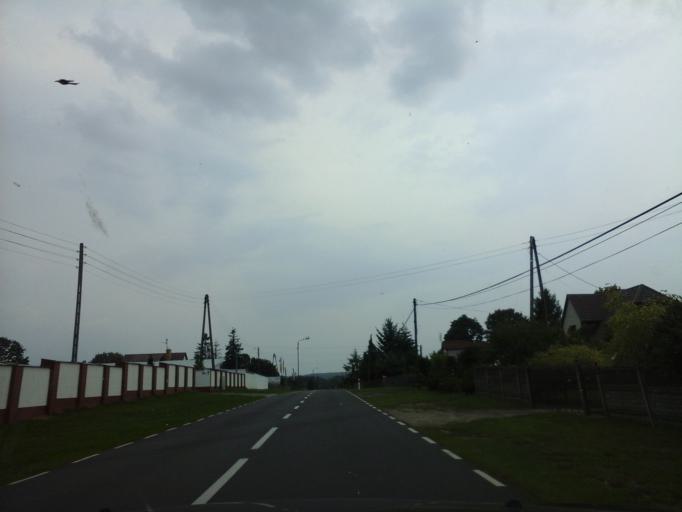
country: PL
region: Lubusz
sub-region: Powiat strzelecko-drezdenecki
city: Dobiegniew
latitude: 52.9425
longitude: 15.7512
